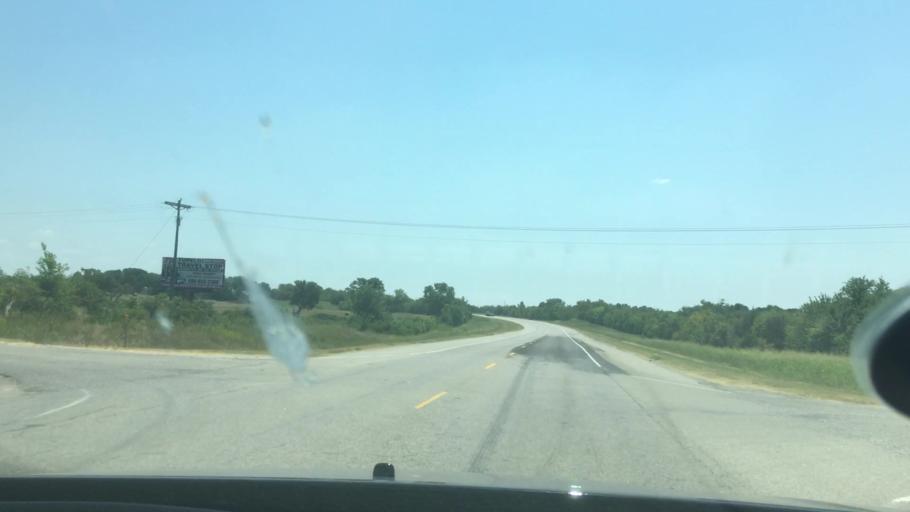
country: US
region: Oklahoma
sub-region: Pontotoc County
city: Ada
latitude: 34.6511
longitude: -96.5541
